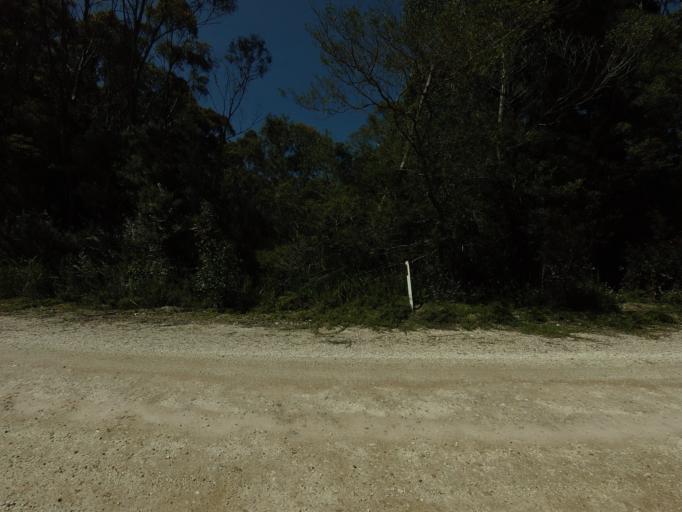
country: AU
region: Tasmania
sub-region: Huon Valley
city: Geeveston
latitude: -42.9955
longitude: 146.3698
